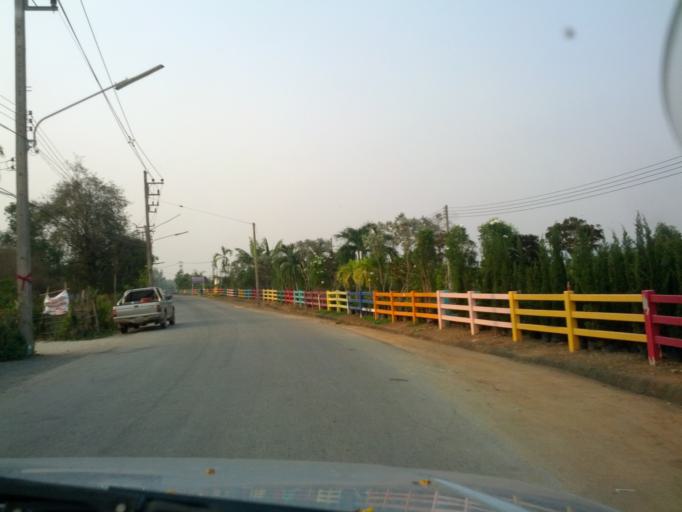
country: TH
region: Chiang Mai
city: San Sai
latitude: 18.9189
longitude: 99.0117
